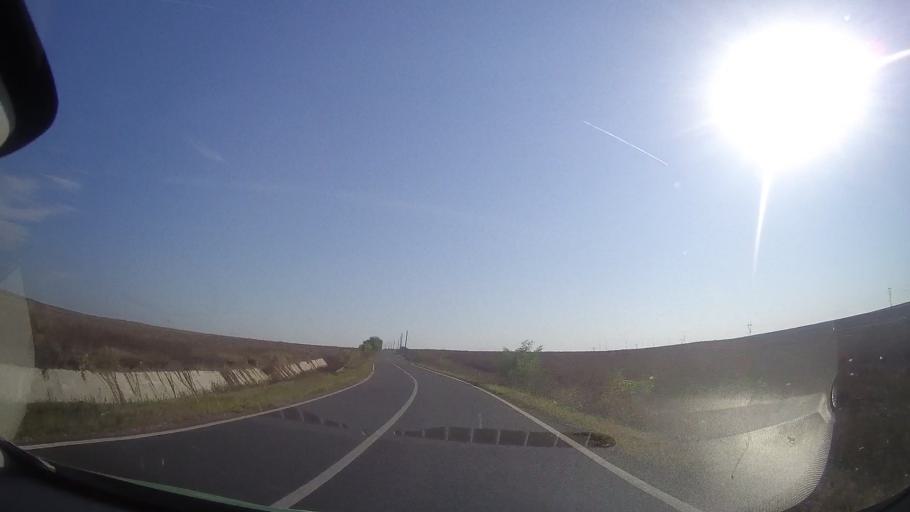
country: RO
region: Timis
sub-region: Oras Recas
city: Recas
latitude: 45.8109
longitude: 21.5591
